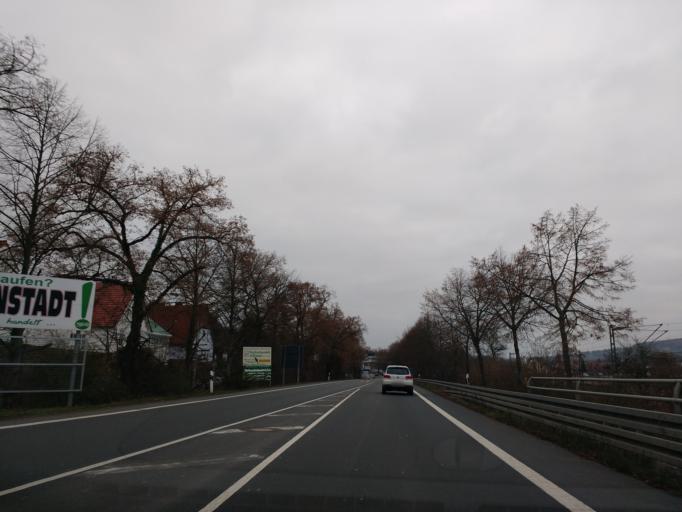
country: DE
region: Hesse
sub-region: Regierungsbezirk Kassel
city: Rotenburg an der Fulda
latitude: 51.0044
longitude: 9.7227
